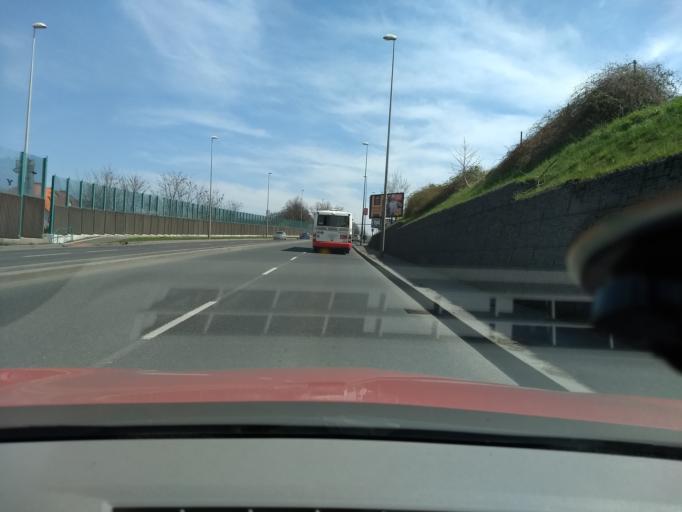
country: CZ
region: Central Bohemia
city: Hostivice
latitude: 50.0768
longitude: 14.3052
